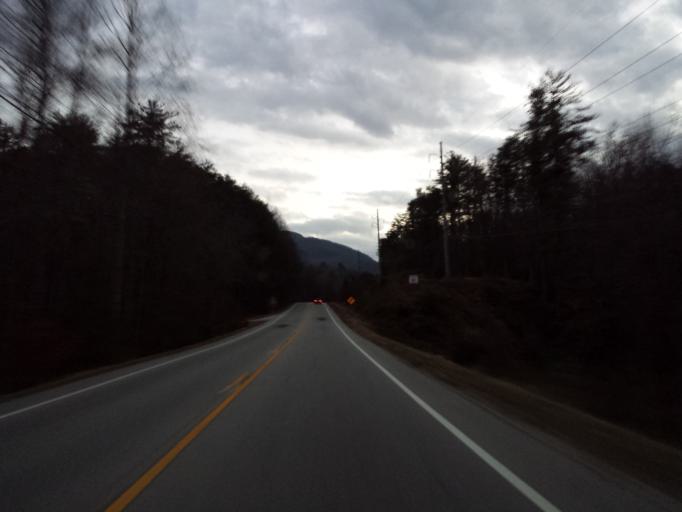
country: US
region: Georgia
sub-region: White County
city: Cleveland
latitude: 34.6725
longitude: -83.7140
